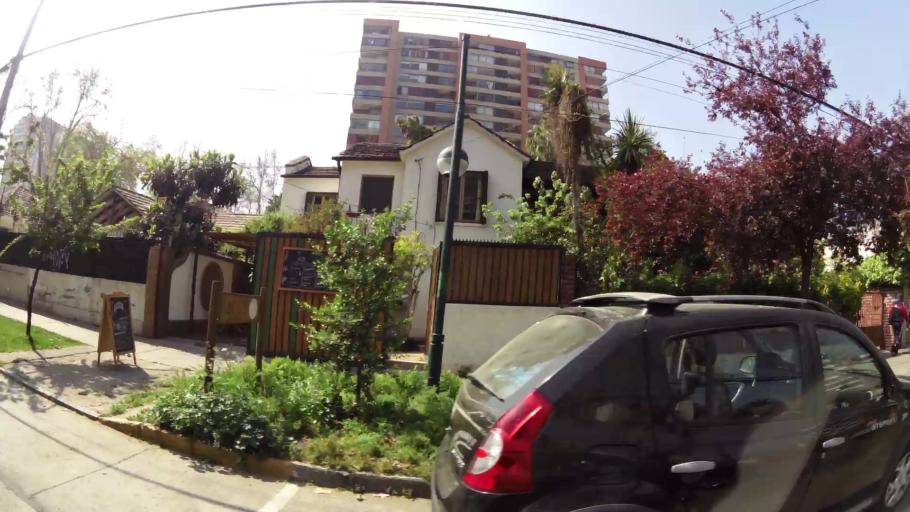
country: CL
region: Santiago Metropolitan
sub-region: Provincia de Santiago
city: Villa Presidente Frei, Nunoa, Santiago, Chile
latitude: -33.4569
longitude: -70.5998
